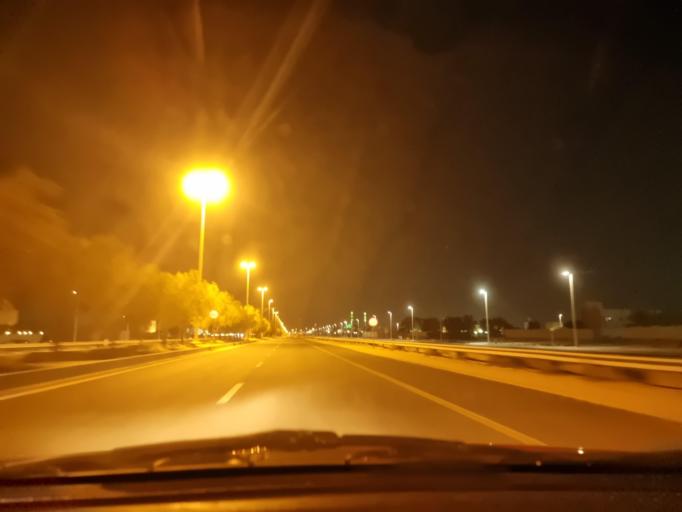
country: AE
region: Abu Dhabi
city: Abu Dhabi
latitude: 24.3693
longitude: 54.7050
